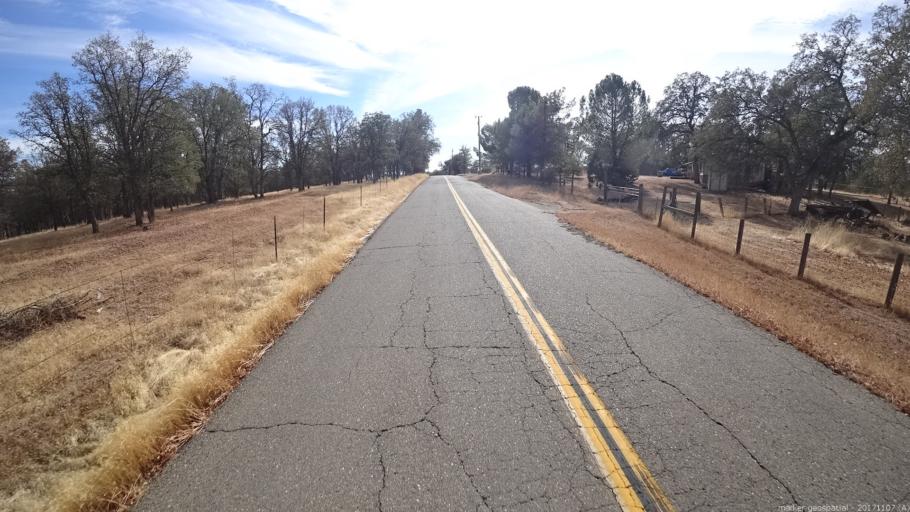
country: US
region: California
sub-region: Shasta County
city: Shasta
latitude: 40.4286
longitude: -122.5209
